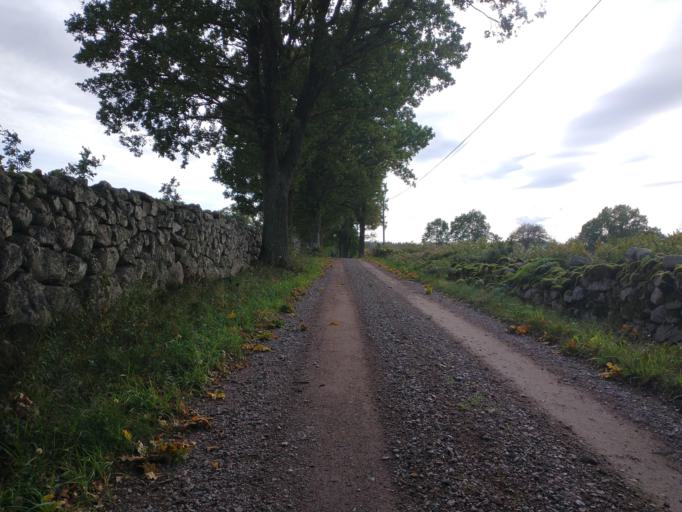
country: SE
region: Kalmar
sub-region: Kalmar Kommun
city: Lindsdal
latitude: 56.7743
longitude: 16.3071
